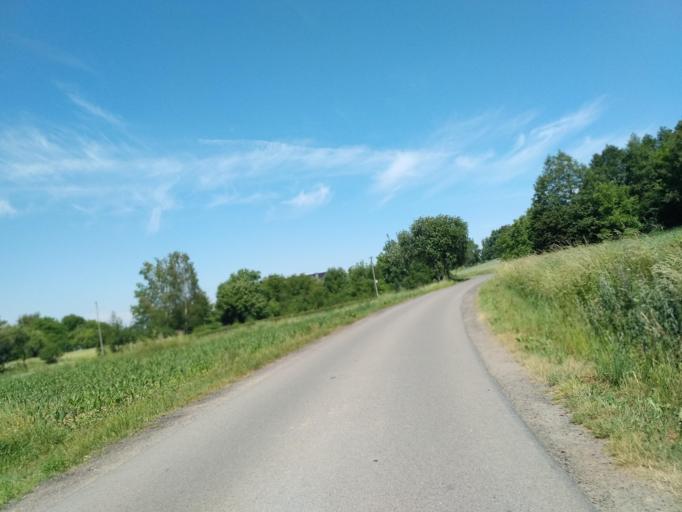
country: PL
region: Subcarpathian Voivodeship
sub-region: Powiat krosnienski
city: Korczyna
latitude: 49.7220
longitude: 21.7799
